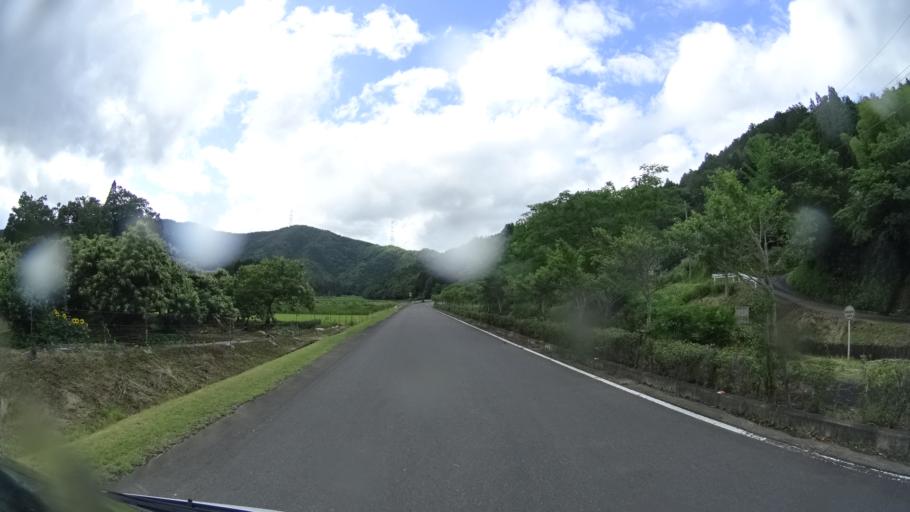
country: JP
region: Kyoto
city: Ayabe
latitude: 35.3487
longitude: 135.1983
